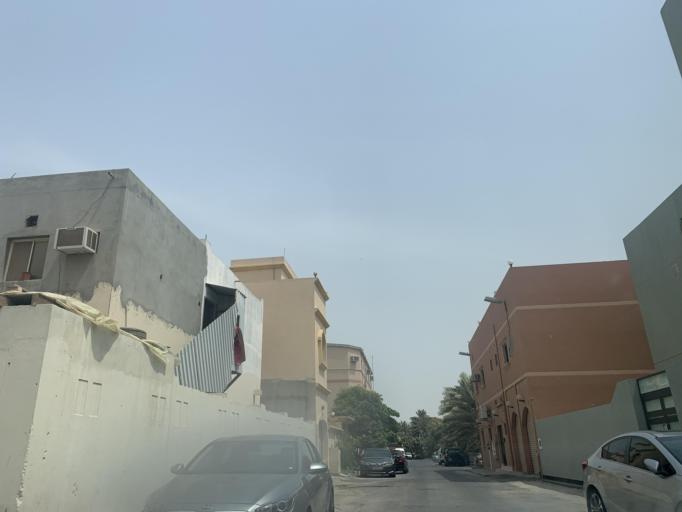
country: BH
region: Manama
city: Jidd Hafs
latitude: 26.1985
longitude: 50.4661
